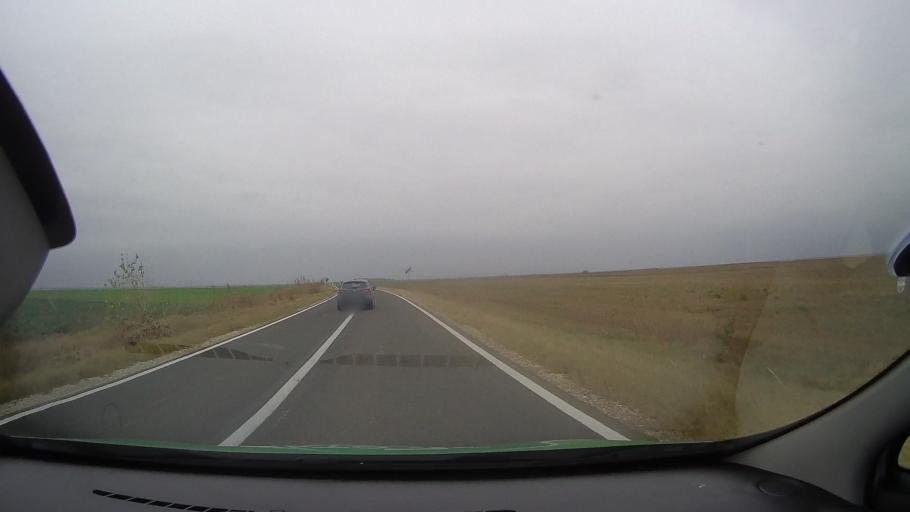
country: RO
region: Constanta
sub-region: Comuna Ciobanu
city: Ciobanu
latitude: 44.7023
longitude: 28.0219
